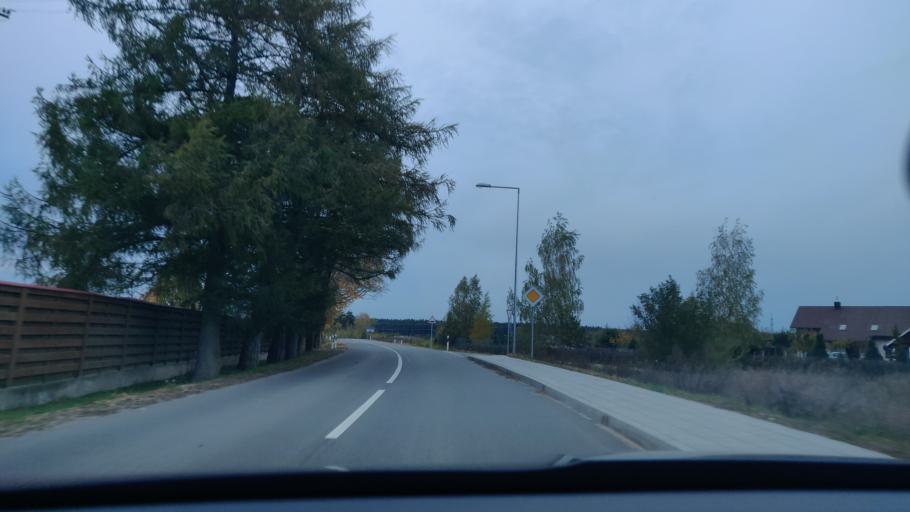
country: LT
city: Lentvaris
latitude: 54.5914
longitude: 25.0481
